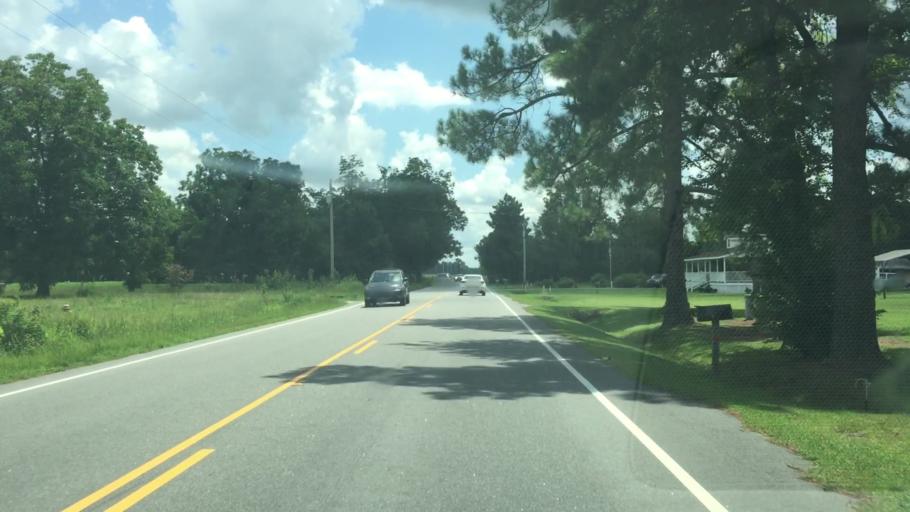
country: US
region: North Carolina
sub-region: Columbus County
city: Chadbourn
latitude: 34.2900
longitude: -78.8243
